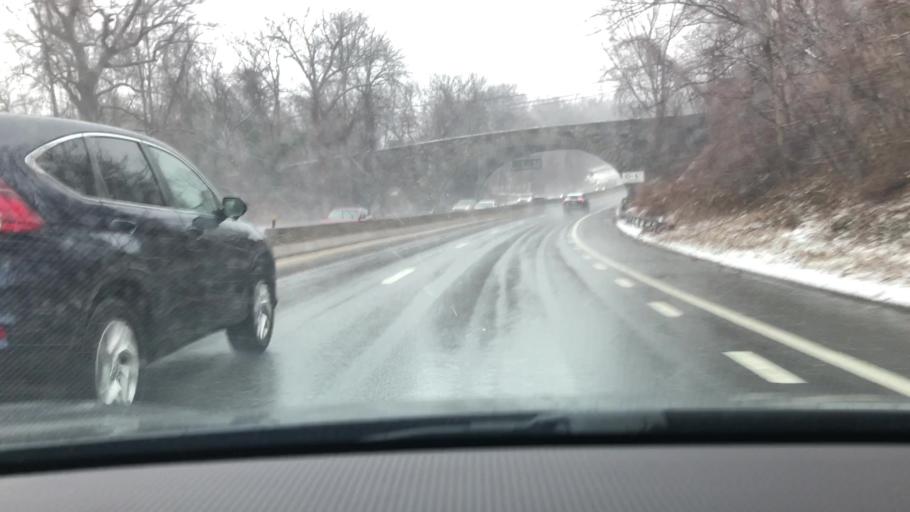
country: US
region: New York
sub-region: Westchester County
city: Tuckahoe
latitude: 40.9545
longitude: -73.7992
